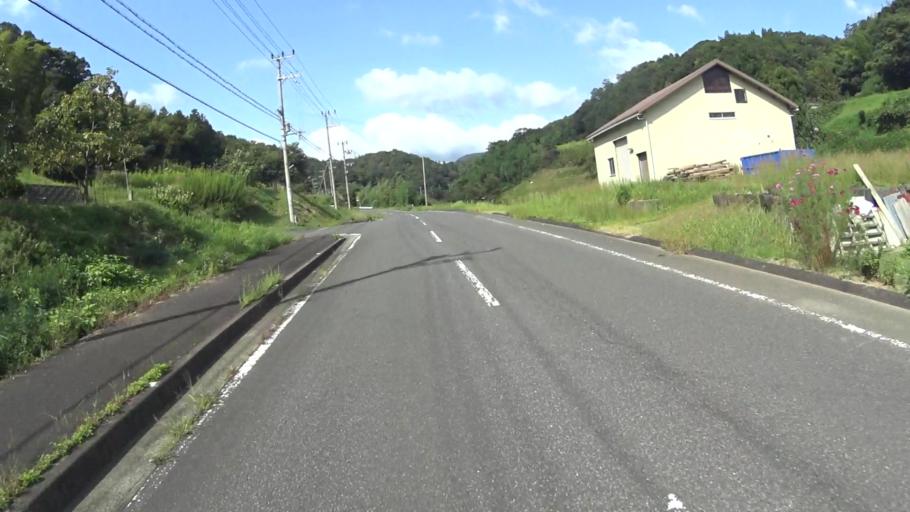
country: JP
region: Kyoto
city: Miyazu
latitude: 35.6266
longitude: 135.2421
